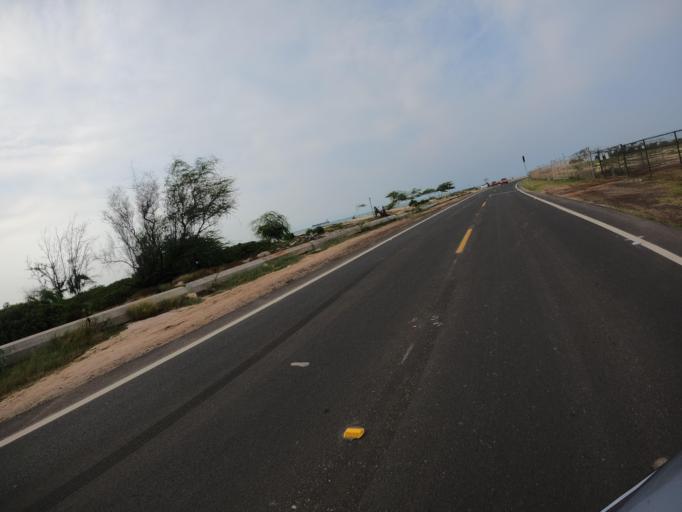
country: US
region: Hawaii
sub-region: Honolulu County
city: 'Ewa Villages
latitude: 21.3012
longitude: -158.0594
